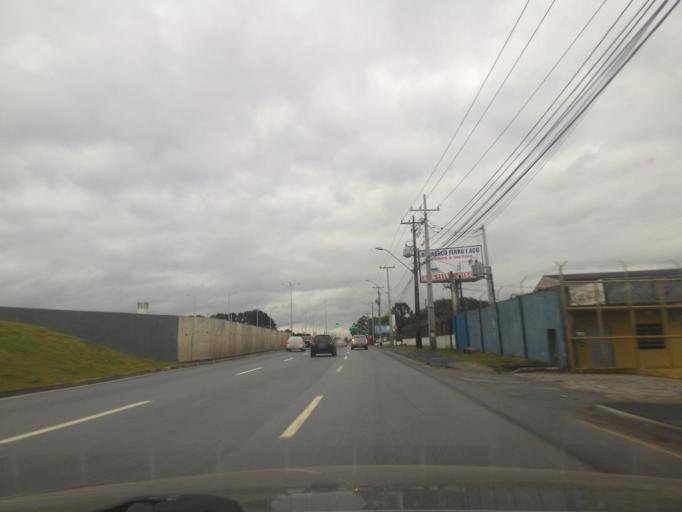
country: BR
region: Parana
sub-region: Sao Jose Dos Pinhais
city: Sao Jose dos Pinhais
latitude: -25.5189
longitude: -49.2926
